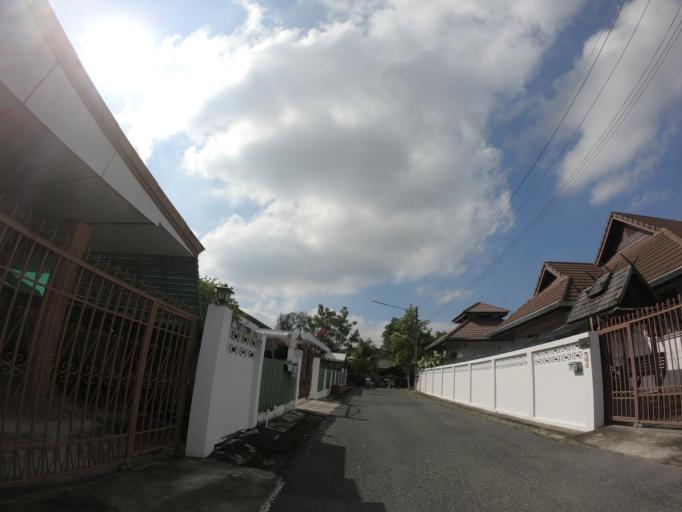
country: TH
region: Chiang Mai
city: Chiang Mai
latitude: 18.7883
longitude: 99.0339
